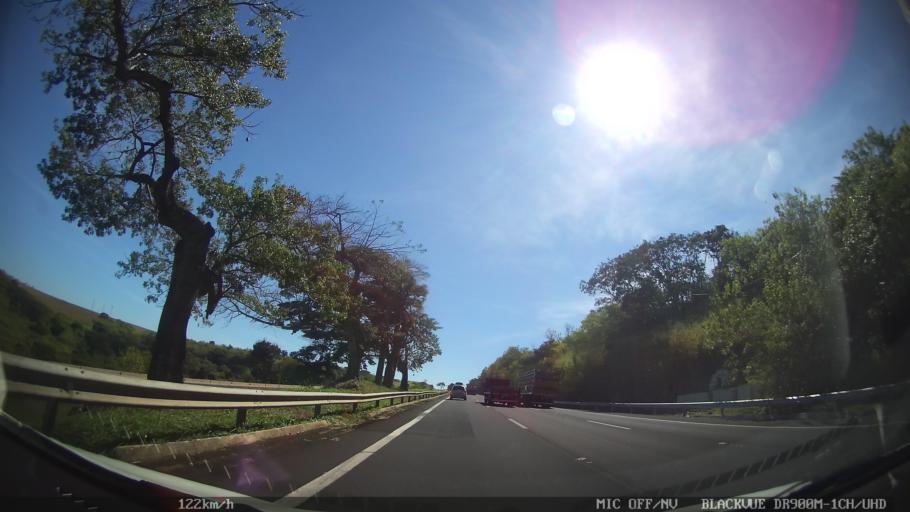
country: BR
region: Sao Paulo
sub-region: Santa Rita Do Passa Quatro
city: Santa Rita do Passa Quatro
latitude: -21.7081
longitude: -47.5931
